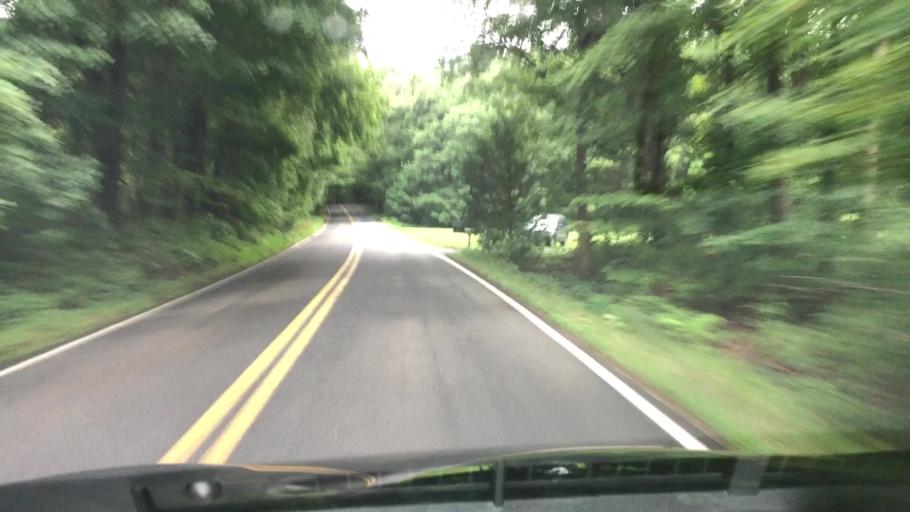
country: US
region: Virginia
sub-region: Fauquier County
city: Bealeton
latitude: 38.5317
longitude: -77.6118
